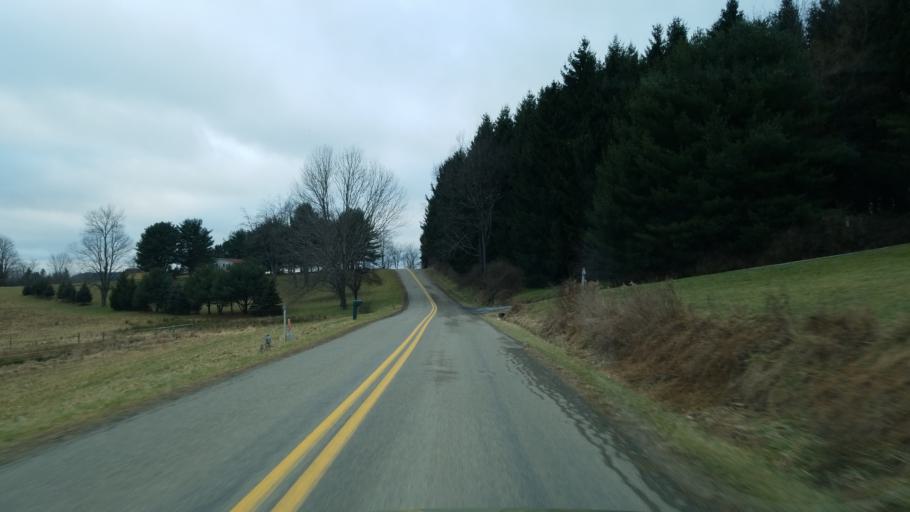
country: US
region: Pennsylvania
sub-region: Jefferson County
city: Falls Creek
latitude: 41.1629
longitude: -78.8141
